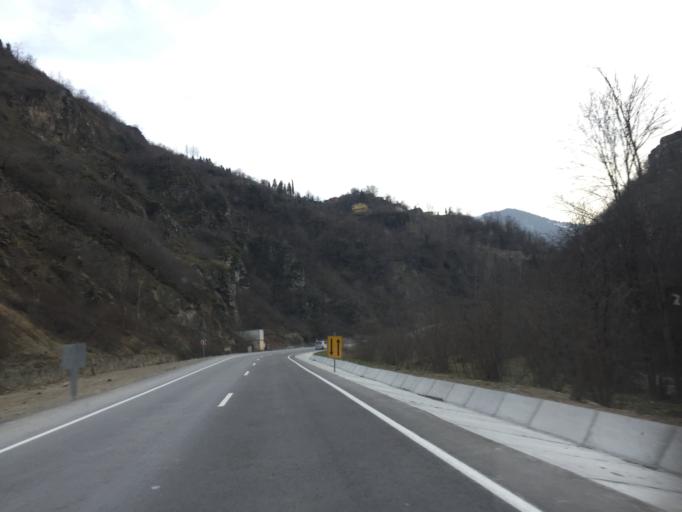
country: TR
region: Trabzon
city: Macka
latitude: 40.7693
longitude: 39.5653
